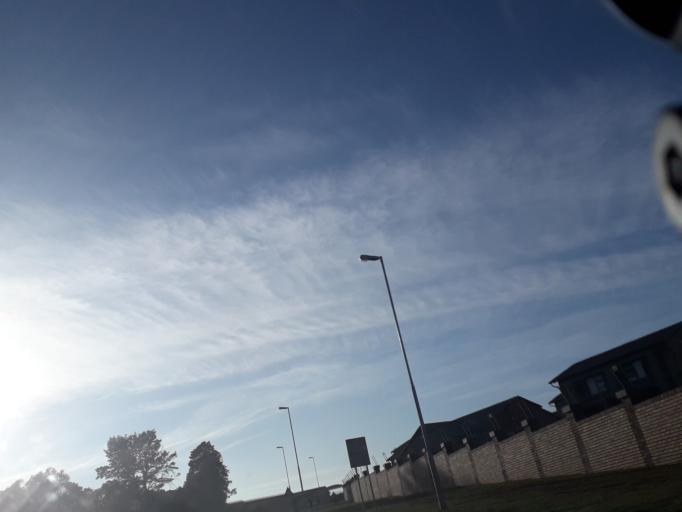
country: ZA
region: Gauteng
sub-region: City of Johannesburg Metropolitan Municipality
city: Roodepoort
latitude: -26.1009
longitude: 27.8942
